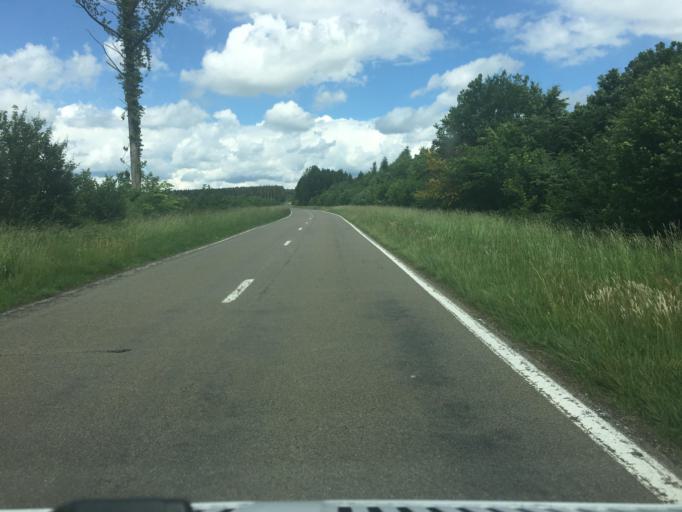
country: BE
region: Wallonia
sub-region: Province du Luxembourg
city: Florenville
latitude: 49.6524
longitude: 5.3377
